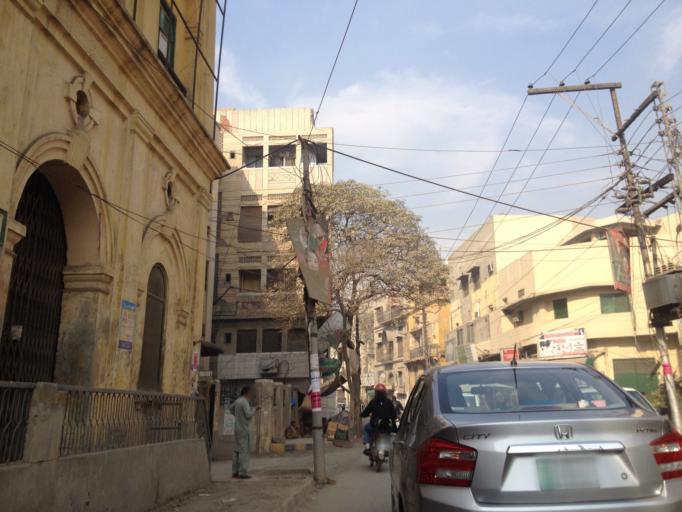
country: PK
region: Punjab
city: Lahore
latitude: 31.5631
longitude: 74.3079
